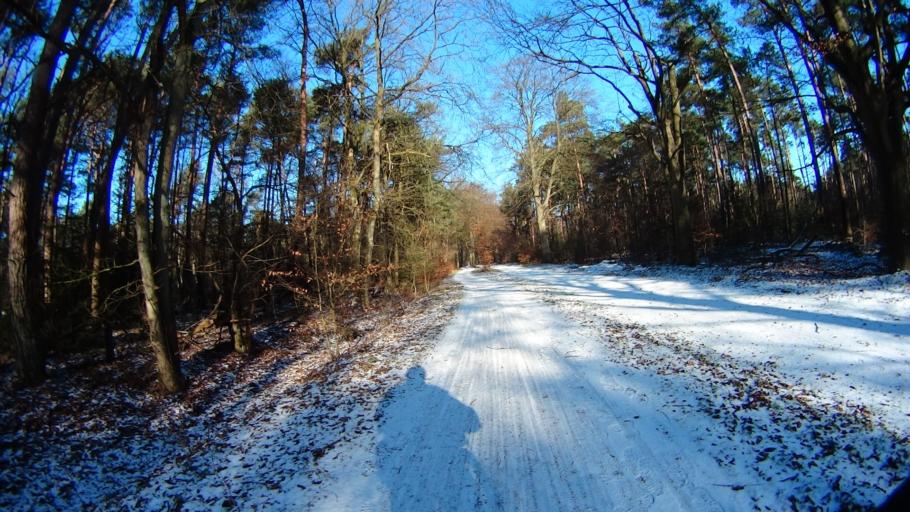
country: NL
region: North Holland
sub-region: Gemeente Hilversum
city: Hilversum
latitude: 52.2091
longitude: 5.2176
